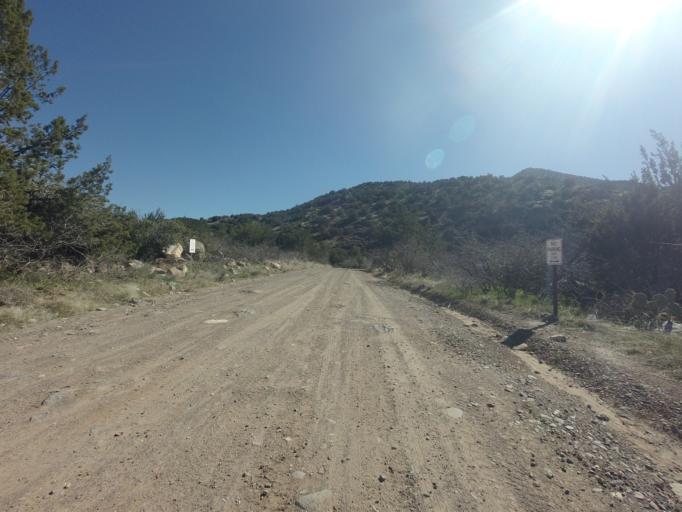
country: US
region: Arizona
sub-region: Gila County
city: Pine
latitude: 34.3940
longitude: -111.6313
